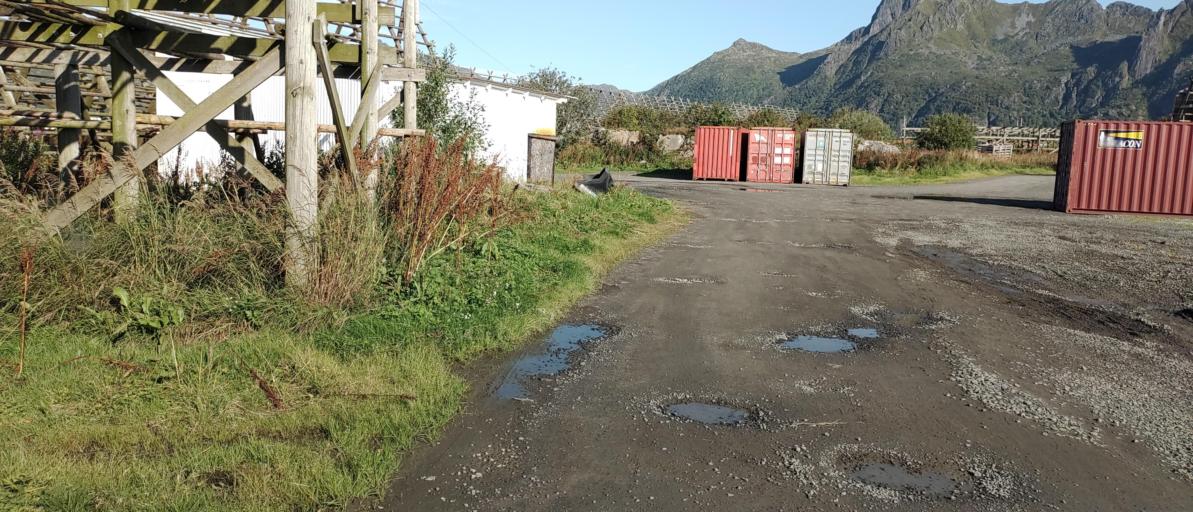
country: NO
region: Nordland
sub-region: Vagan
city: Svolvaer
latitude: 68.2264
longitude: 14.5692
